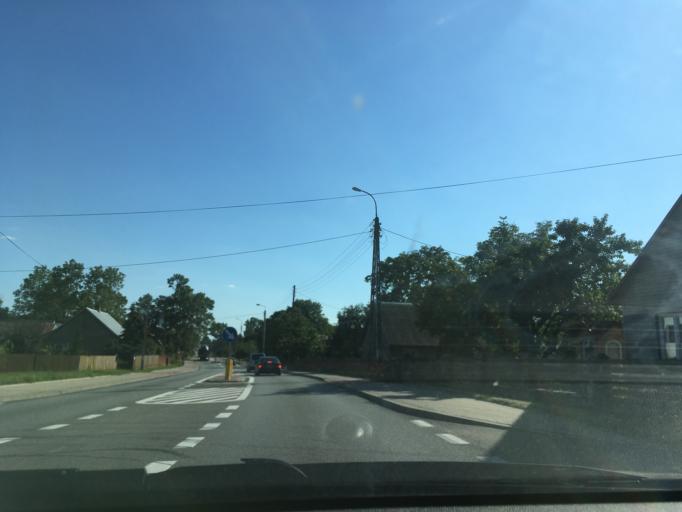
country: PL
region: Podlasie
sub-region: Powiat sokolski
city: Suchowola
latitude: 53.5099
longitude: 23.0997
